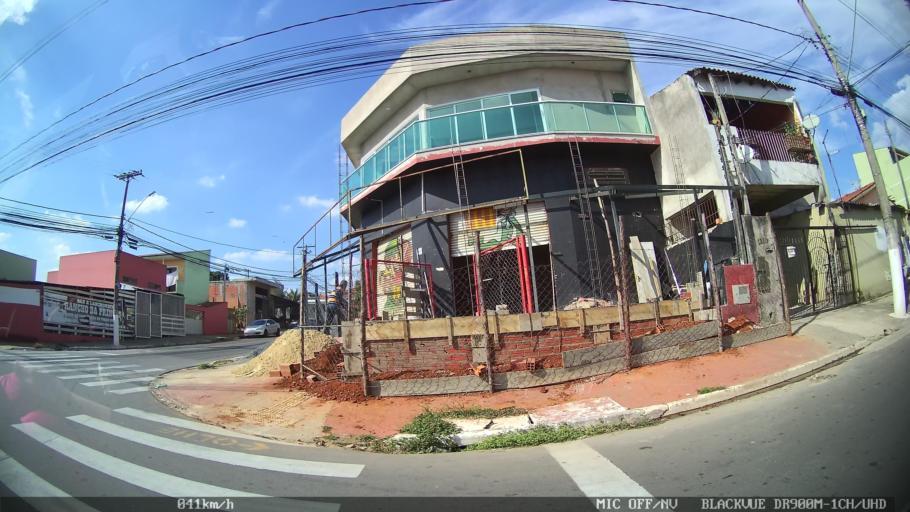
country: BR
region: Sao Paulo
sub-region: Hortolandia
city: Hortolandia
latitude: -22.8942
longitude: -47.2348
